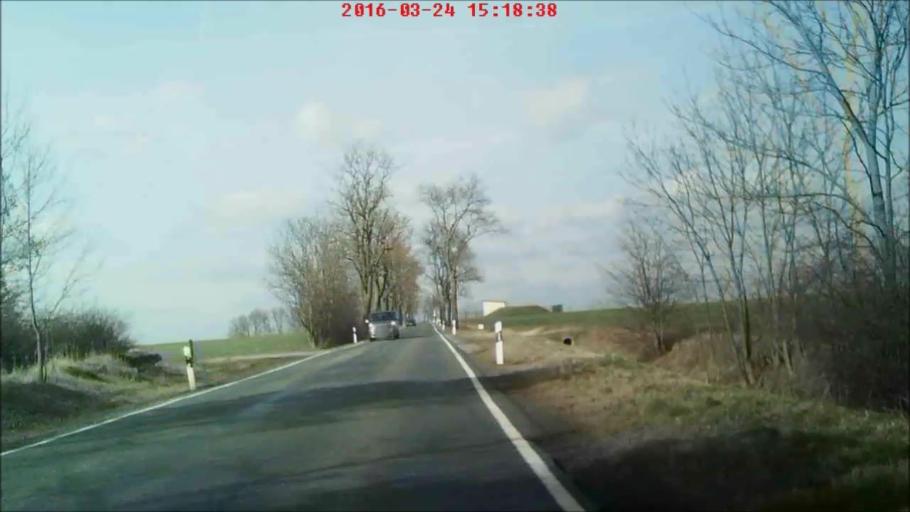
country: DE
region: Thuringia
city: Stadtilm
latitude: 50.7953
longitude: 11.0705
